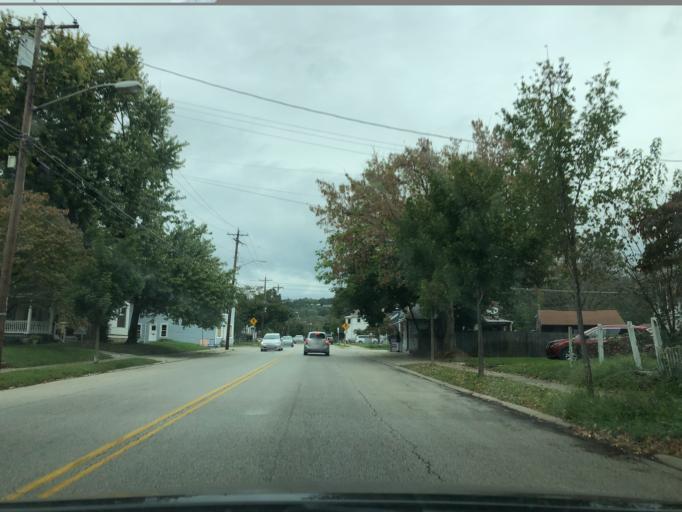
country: US
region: Ohio
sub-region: Hamilton County
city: Mariemont
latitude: 39.1532
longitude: -84.3803
